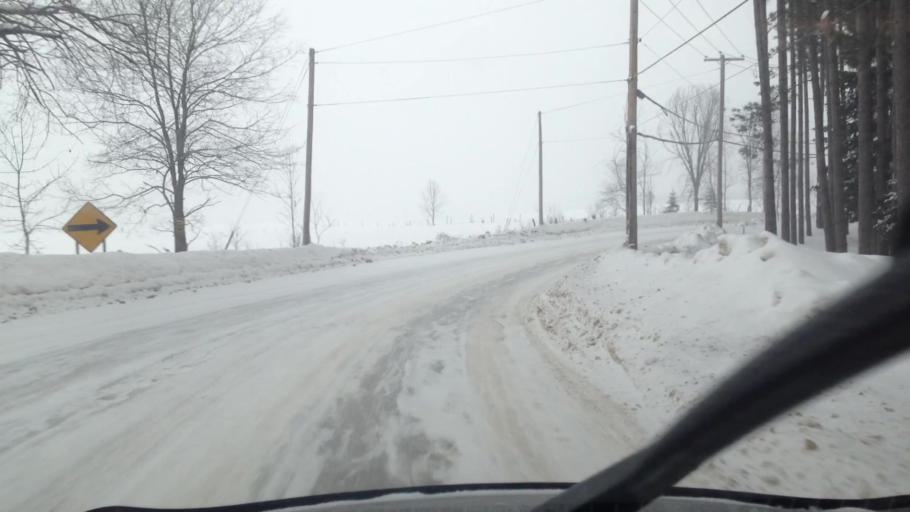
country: CA
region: Quebec
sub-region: Laurentides
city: Mont-Tremblant
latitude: 45.9726
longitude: -74.6294
